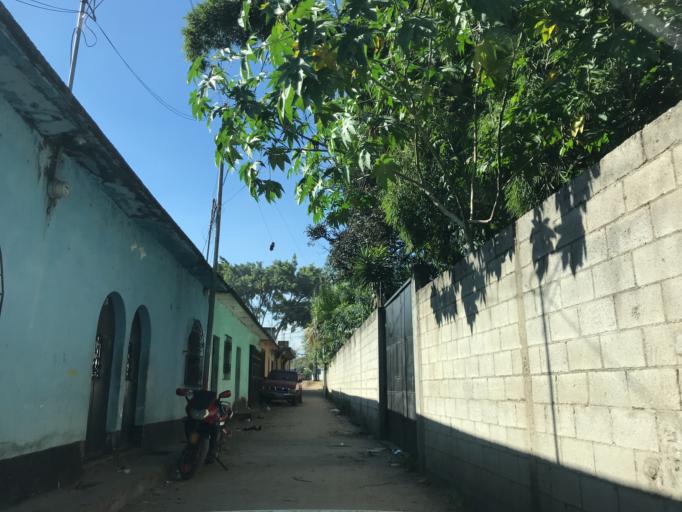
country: GT
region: Guatemala
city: Petapa
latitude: 14.4922
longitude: -90.5556
